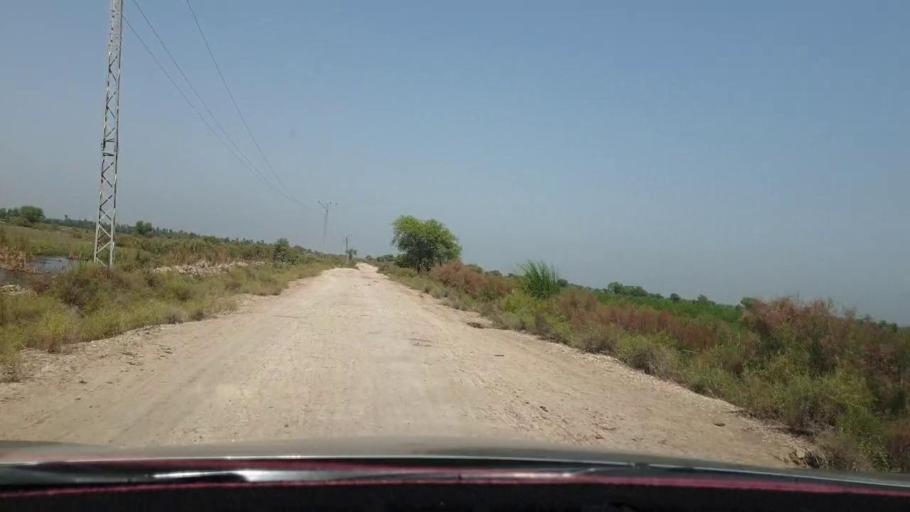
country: PK
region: Sindh
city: Warah
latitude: 27.3987
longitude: 67.6881
